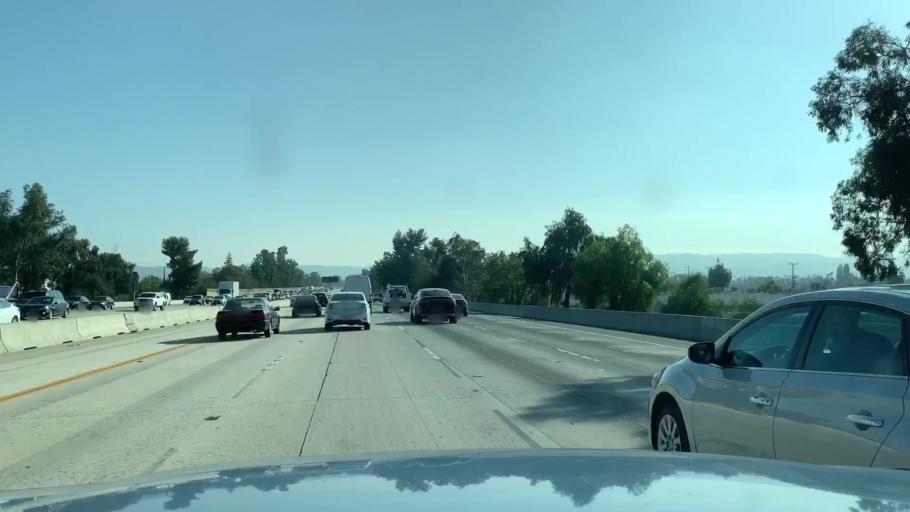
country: US
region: California
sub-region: Los Angeles County
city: Van Nuys
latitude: 34.2144
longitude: -118.4734
